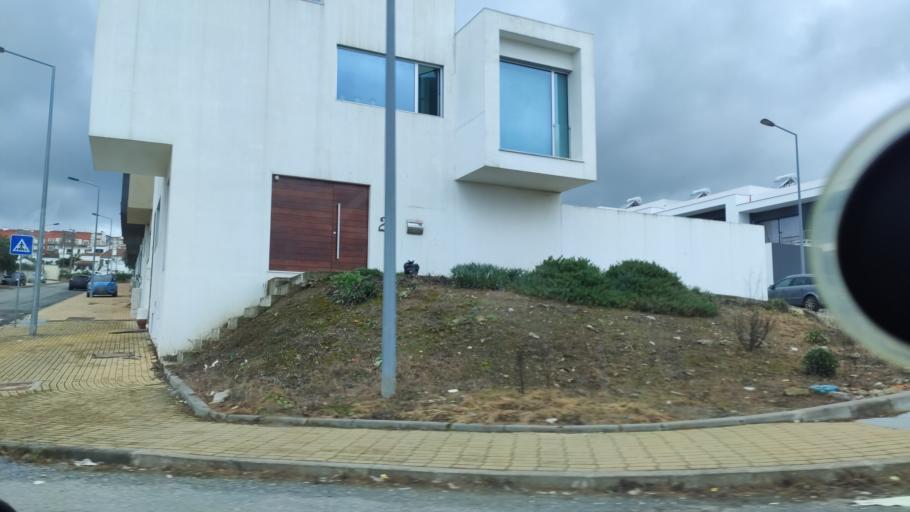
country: PT
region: Beja
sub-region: Beja
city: Beja
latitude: 38.0159
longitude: -7.8527
